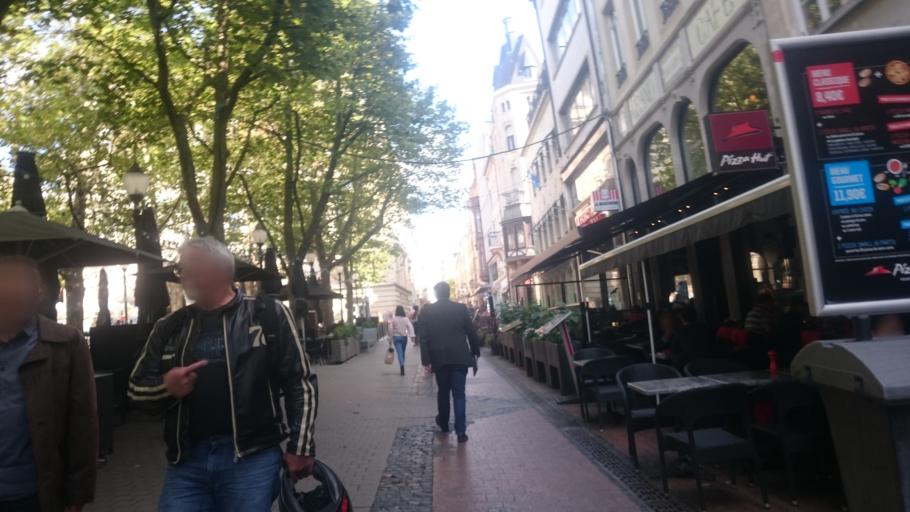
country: LU
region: Luxembourg
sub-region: Canton de Luxembourg
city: Luxembourg
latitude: 49.6110
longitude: 6.1291
